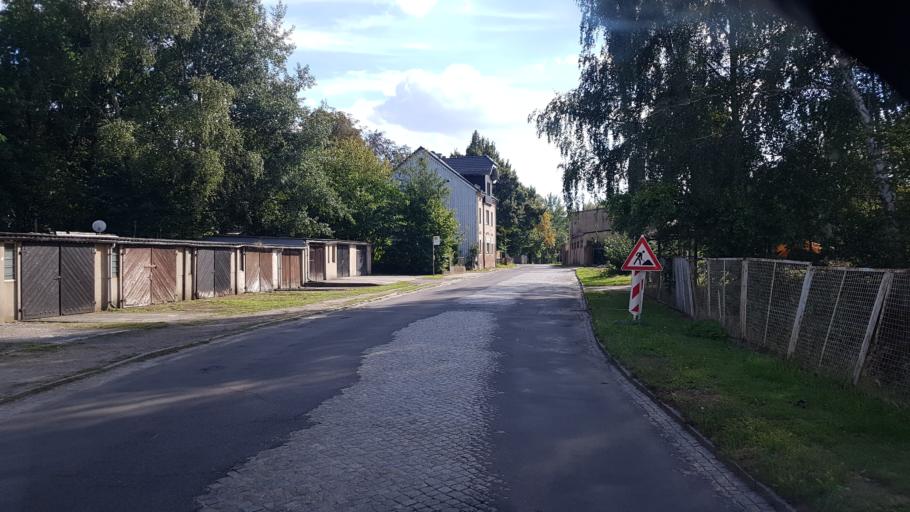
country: DE
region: Brandenburg
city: Tschernitz
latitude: 51.6123
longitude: 14.5920
